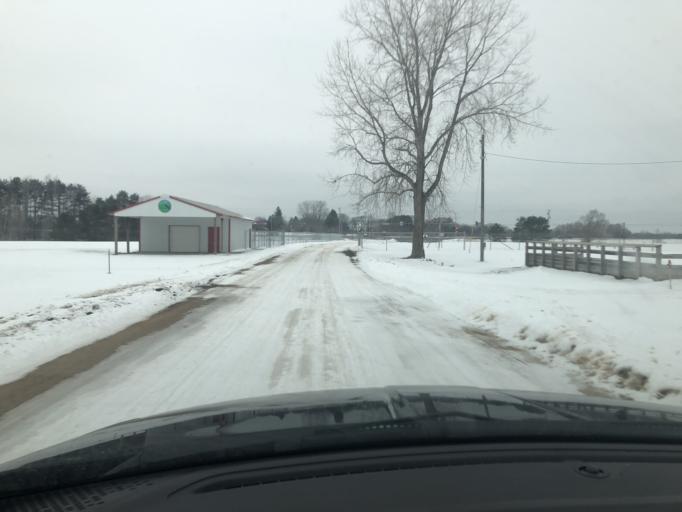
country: US
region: Minnesota
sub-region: Washington County
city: Lake Elmo
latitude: 45.0104
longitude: -92.8598
